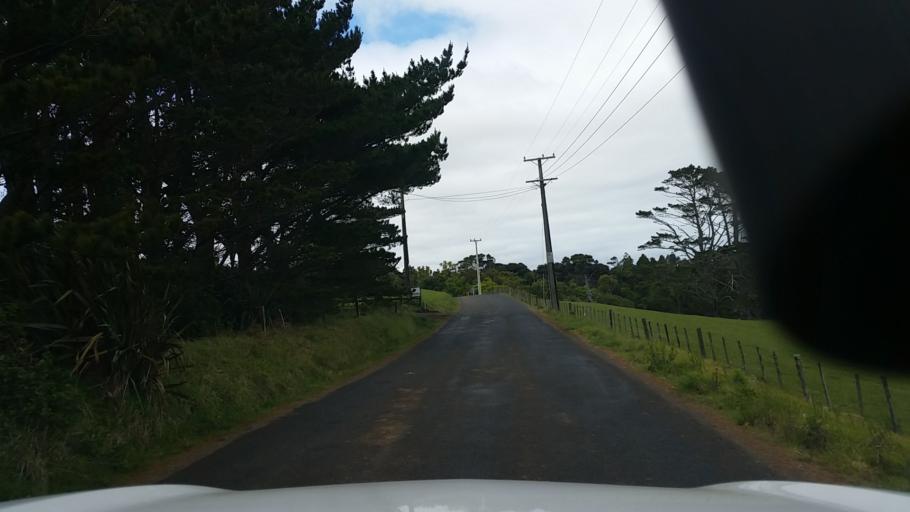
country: NZ
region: Auckland
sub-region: Auckland
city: Muriwai Beach
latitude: -36.8532
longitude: 174.4837
